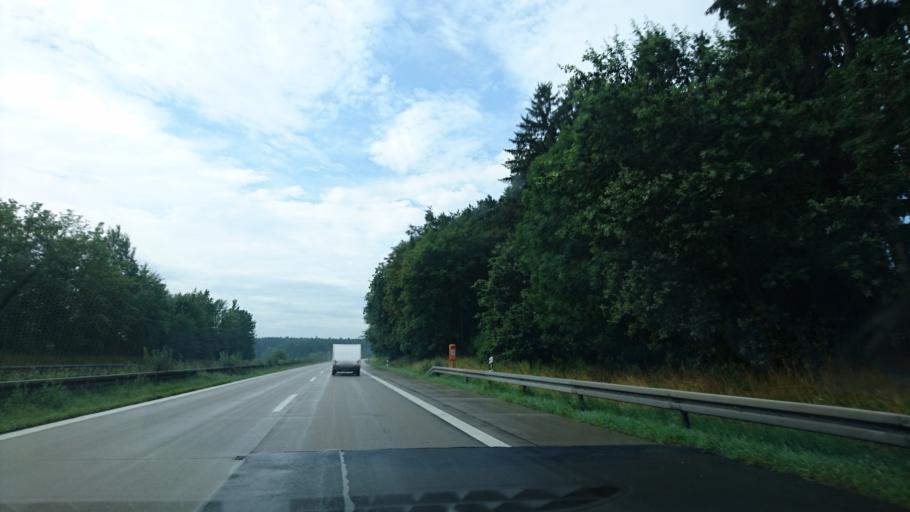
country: DE
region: Bavaria
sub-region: Lower Bavaria
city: Bad Abbach
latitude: 48.9161
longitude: 12.0881
